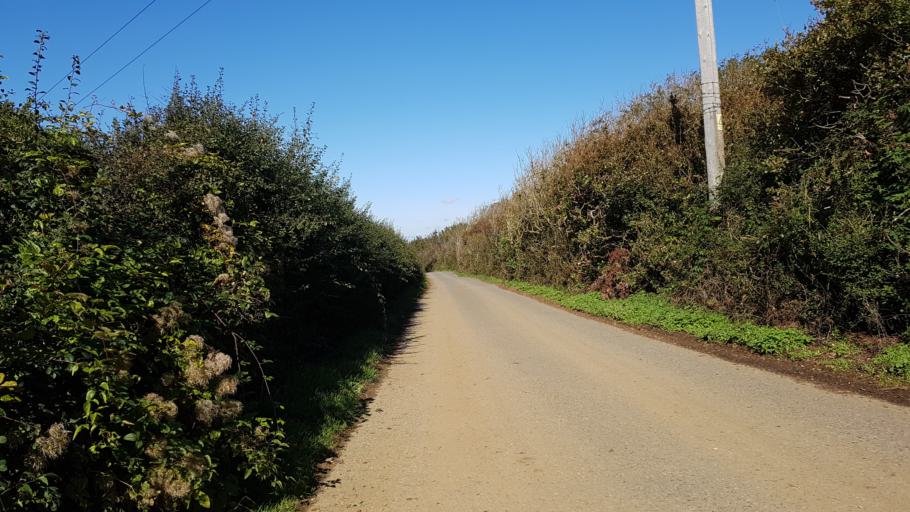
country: GB
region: England
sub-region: Isle of Wight
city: Newport
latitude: 50.6846
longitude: -1.2806
